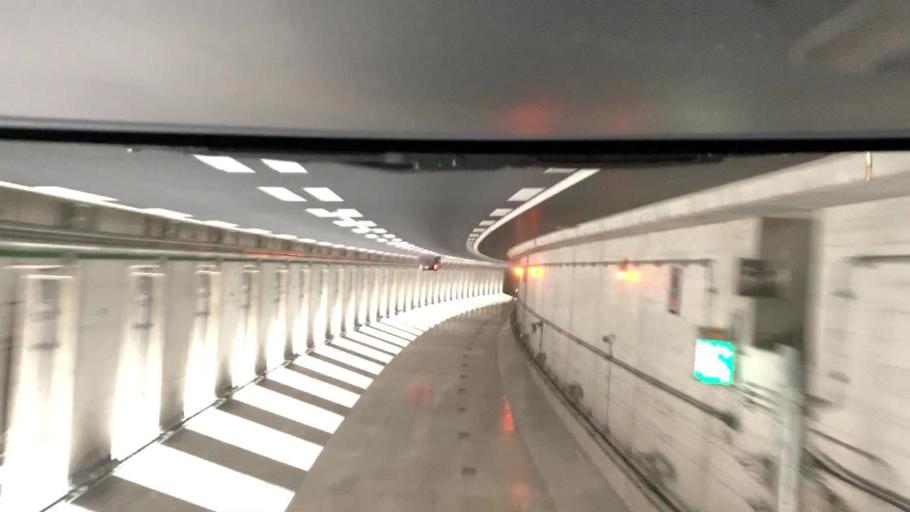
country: JP
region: Chiba
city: Matsudo
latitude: 35.7550
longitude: 139.9143
